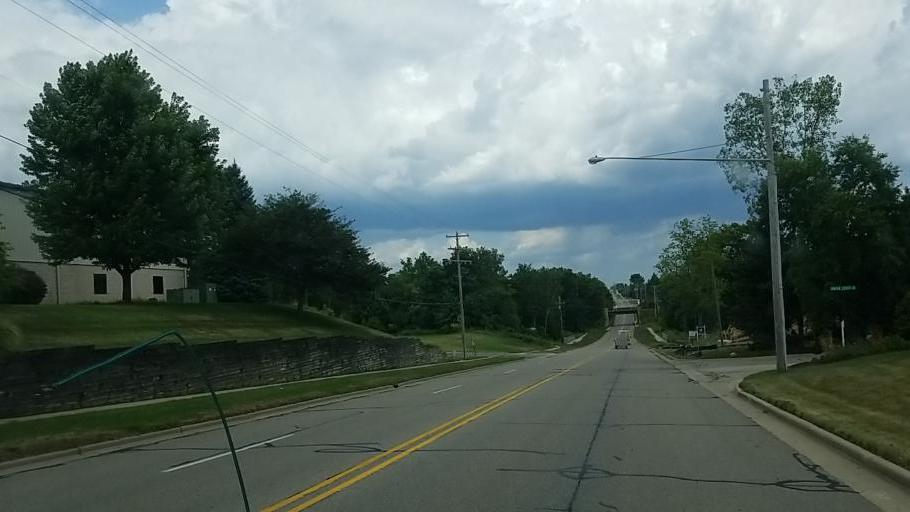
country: US
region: Michigan
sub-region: Kent County
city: Walker
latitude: 43.0152
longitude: -85.7363
